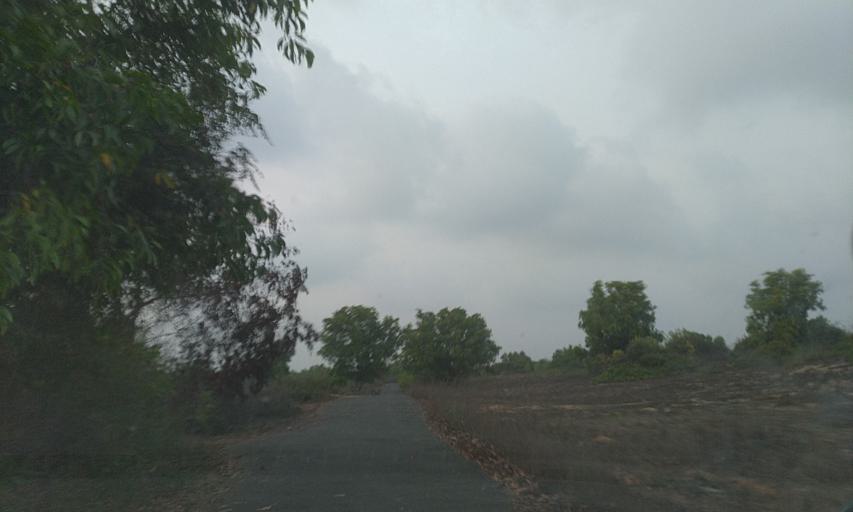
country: IN
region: Goa
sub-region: South Goa
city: Cavelossim
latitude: 15.1878
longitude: 73.9422
